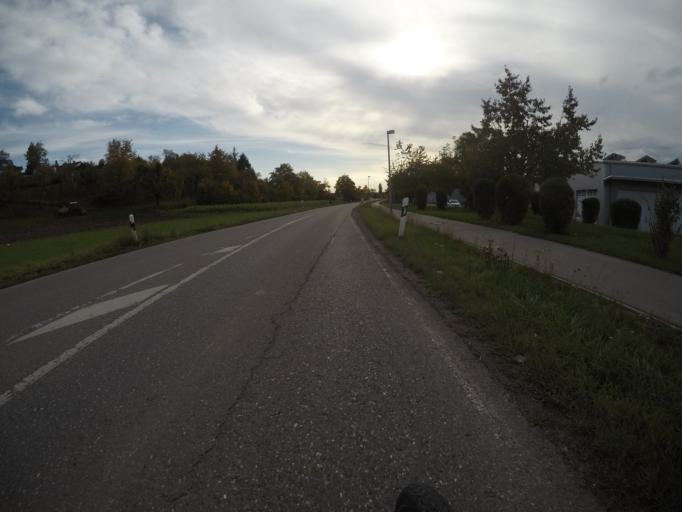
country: DE
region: Baden-Wuerttemberg
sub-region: Regierungsbezirk Stuttgart
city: Herrenberg
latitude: 48.5645
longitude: 8.9086
